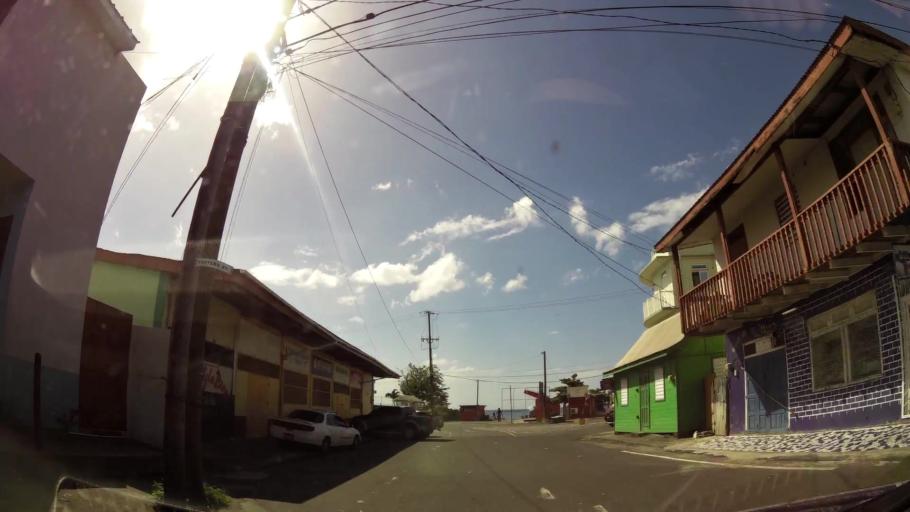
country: DM
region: Saint George
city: Roseau
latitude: 15.3005
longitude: -61.3899
